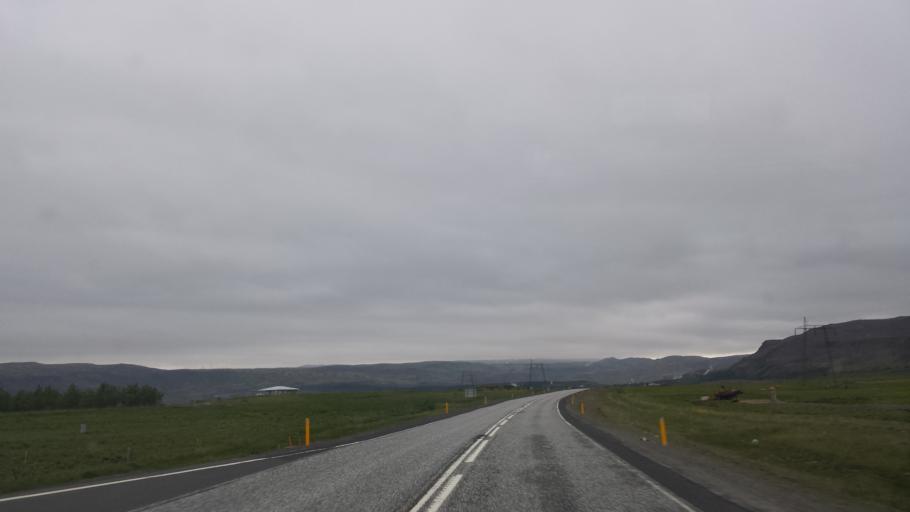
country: IS
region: South
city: Hveragerdi
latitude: 63.9775
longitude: -21.1485
